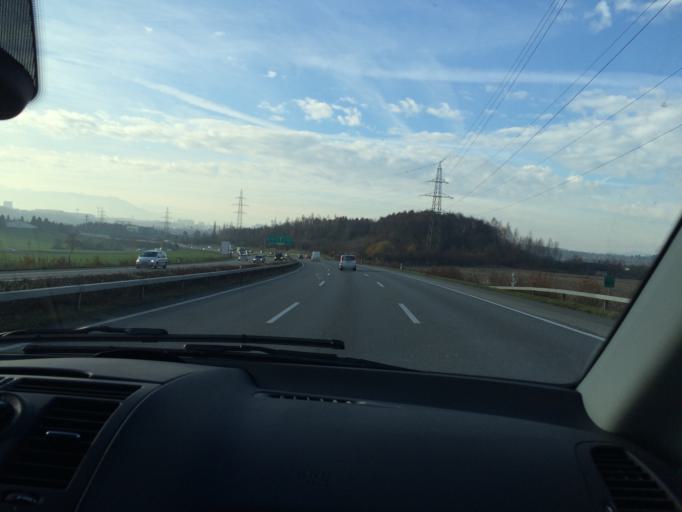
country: CH
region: Bern
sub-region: Bern-Mittelland District
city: Zollikofen
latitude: 46.9871
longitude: 7.4697
